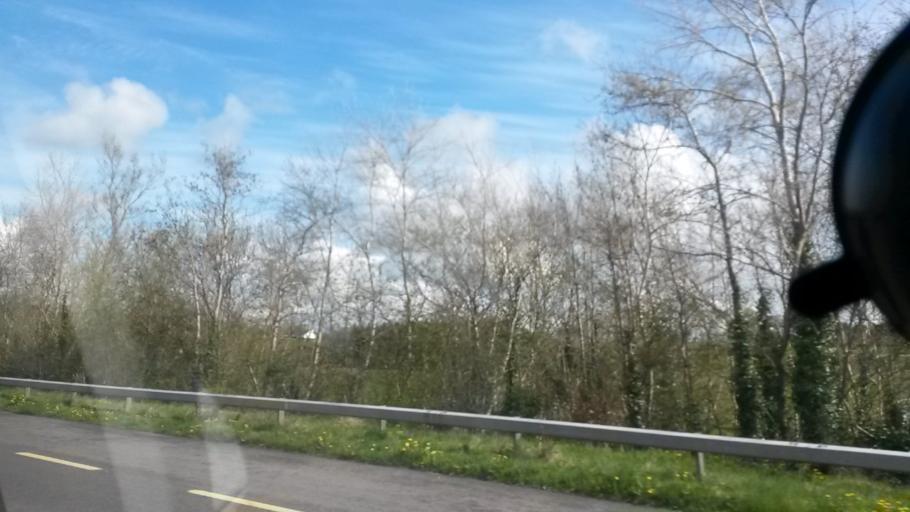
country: IE
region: Ulster
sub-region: An Cabhan
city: Belturbet
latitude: 54.1007
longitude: -7.4626
